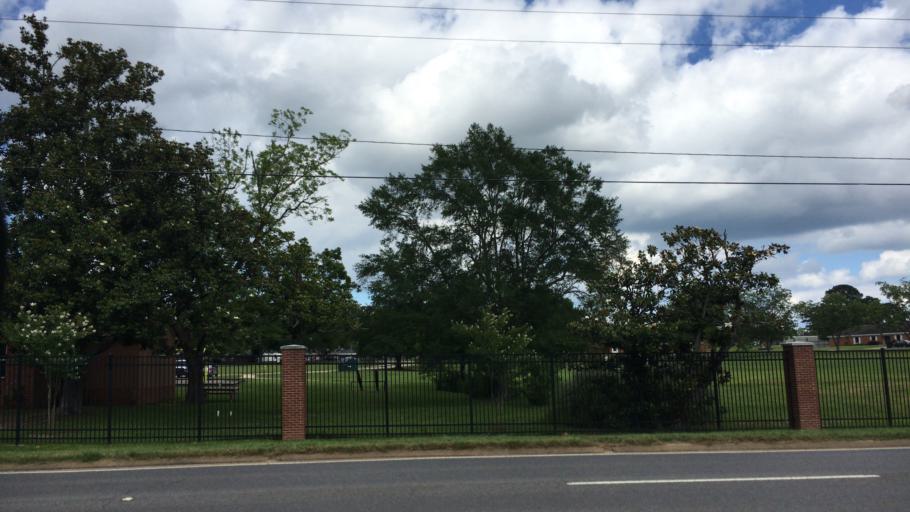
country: US
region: Louisiana
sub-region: Lincoln Parish
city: Ruston
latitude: 32.5179
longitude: -92.6387
